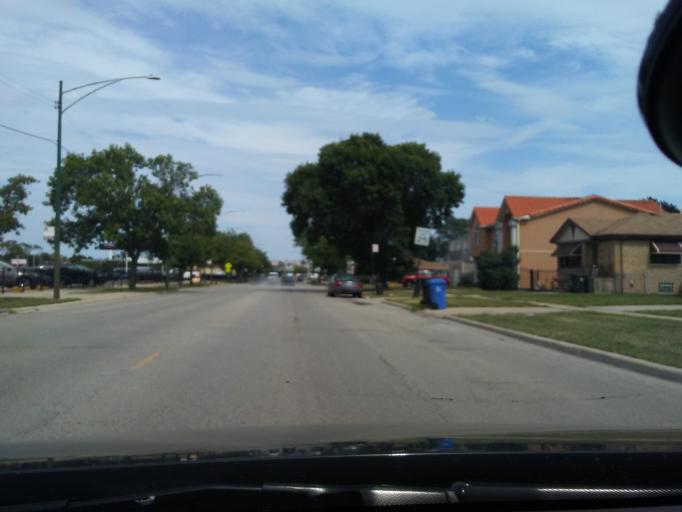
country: US
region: Illinois
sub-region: Cook County
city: Harwood Heights
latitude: 41.9745
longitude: -87.8106
